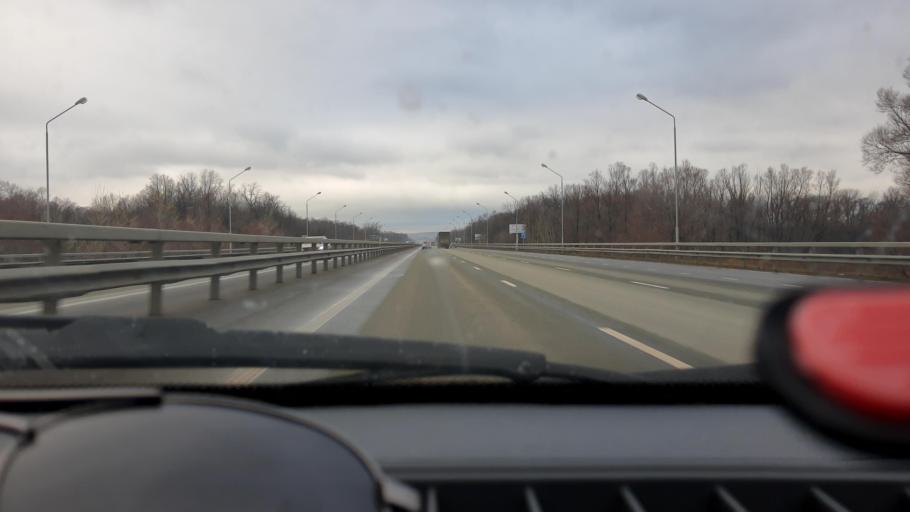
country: RU
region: Bashkortostan
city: Ufa
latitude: 54.6651
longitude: 55.8611
